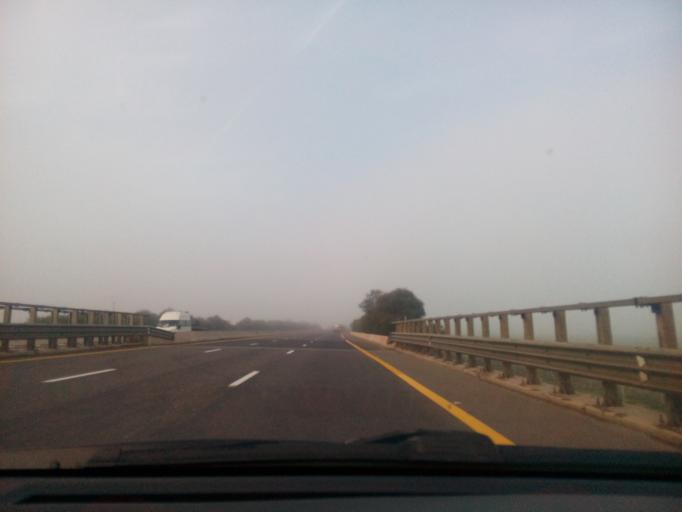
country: DZ
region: Relizane
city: Relizane
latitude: 35.7908
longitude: 0.4667
